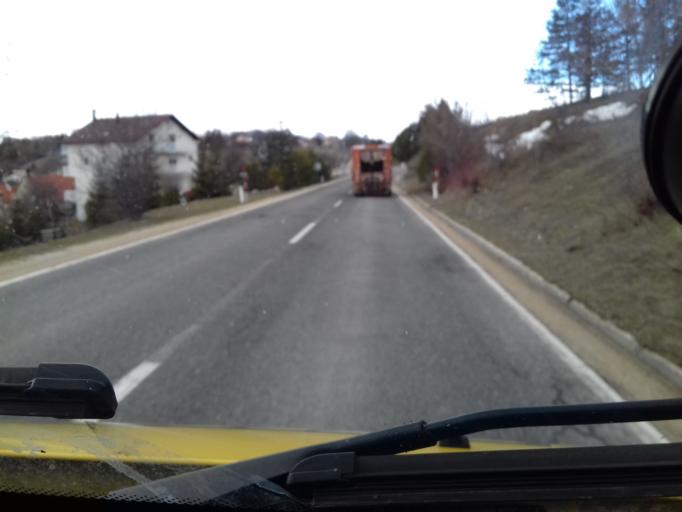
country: BA
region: Federation of Bosnia and Herzegovina
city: Tomislavgrad
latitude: 43.7269
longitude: 17.2241
